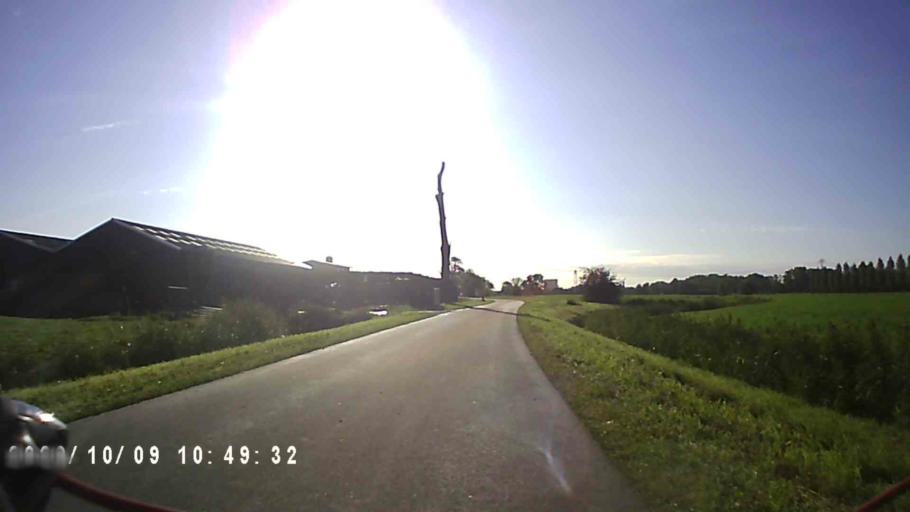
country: NL
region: Groningen
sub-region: Gemeente Groningen
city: Korrewegwijk
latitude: 53.2526
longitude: 6.5467
